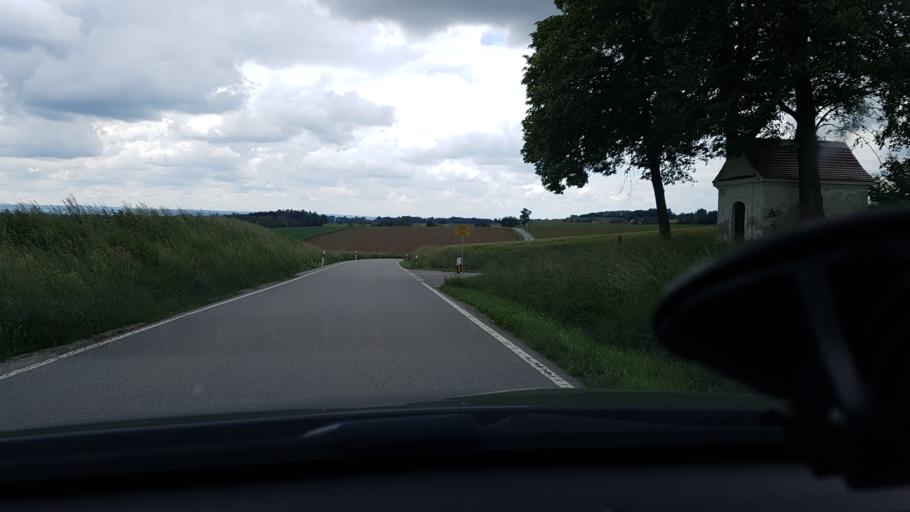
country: DE
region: Bavaria
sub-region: Lower Bavaria
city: Rotthalmunster
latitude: 48.3502
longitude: 13.1999
